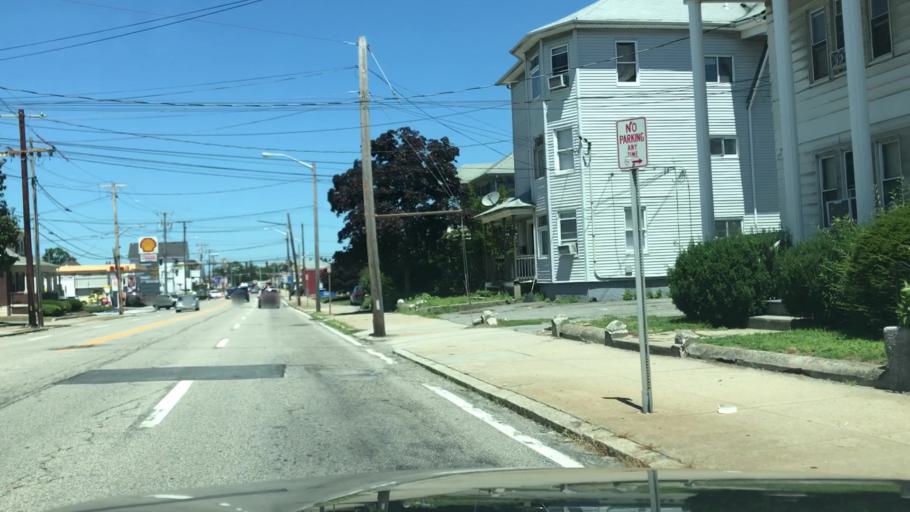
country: US
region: Massachusetts
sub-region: Bristol County
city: North Seekonk
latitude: 41.8908
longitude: -71.3540
